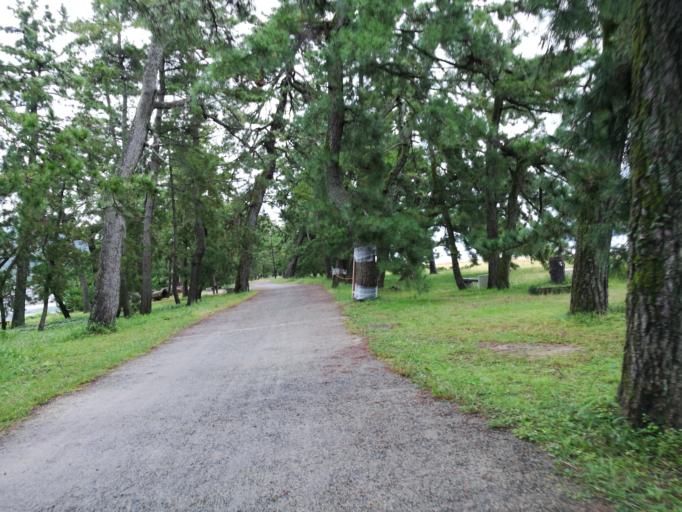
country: JP
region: Kyoto
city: Miyazu
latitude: 35.5755
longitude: 135.1964
